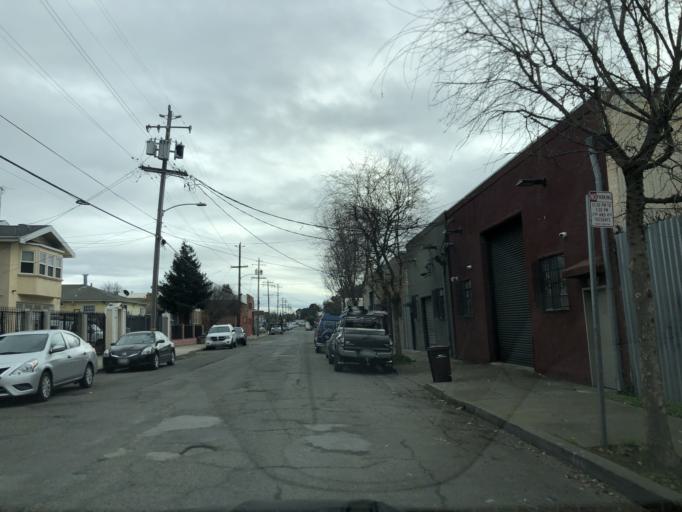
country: US
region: California
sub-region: Alameda County
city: San Leandro
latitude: 37.7357
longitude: -122.1780
